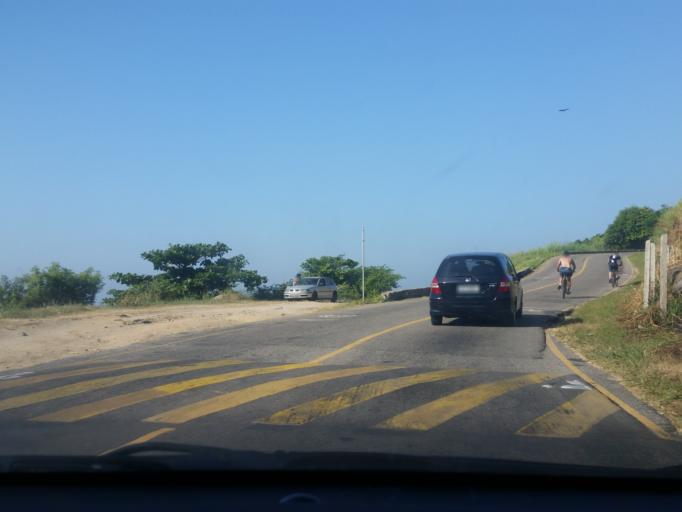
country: BR
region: Rio de Janeiro
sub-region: Nilopolis
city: Nilopolis
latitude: -23.0336
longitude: -43.4930
